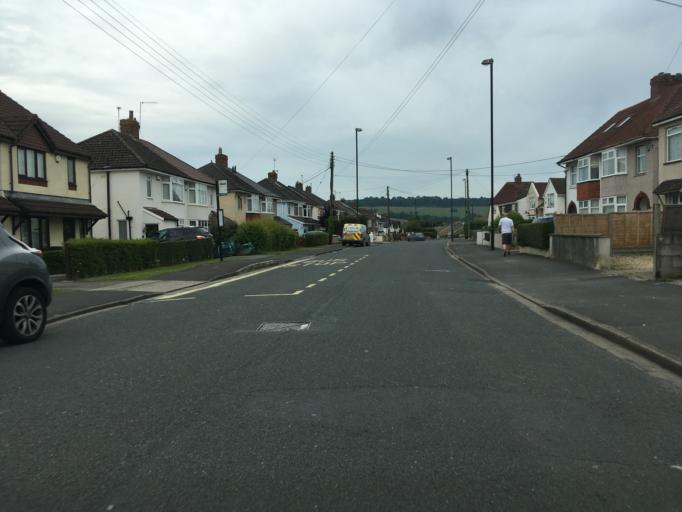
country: GB
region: England
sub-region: Bath and North East Somerset
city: Whitchurch
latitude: 51.4098
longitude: -2.5627
